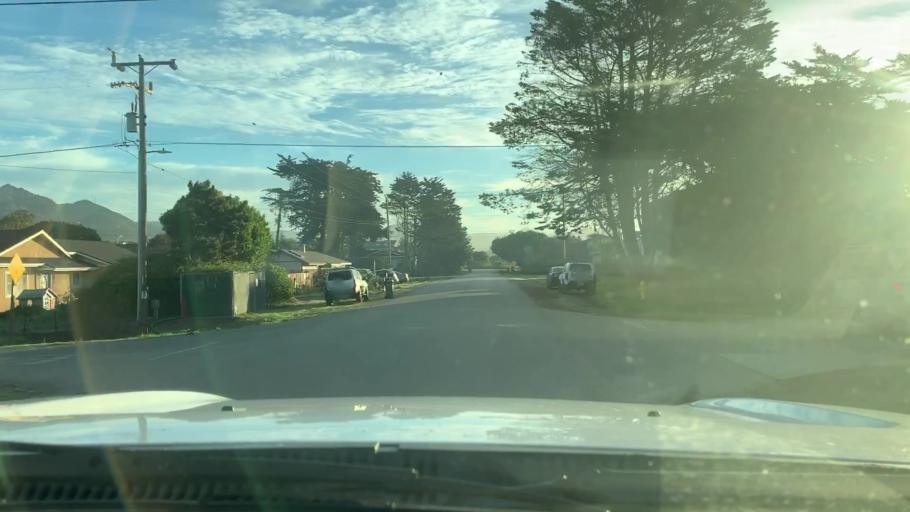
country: US
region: California
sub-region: San Luis Obispo County
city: Los Osos
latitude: 35.3244
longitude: -120.8257
